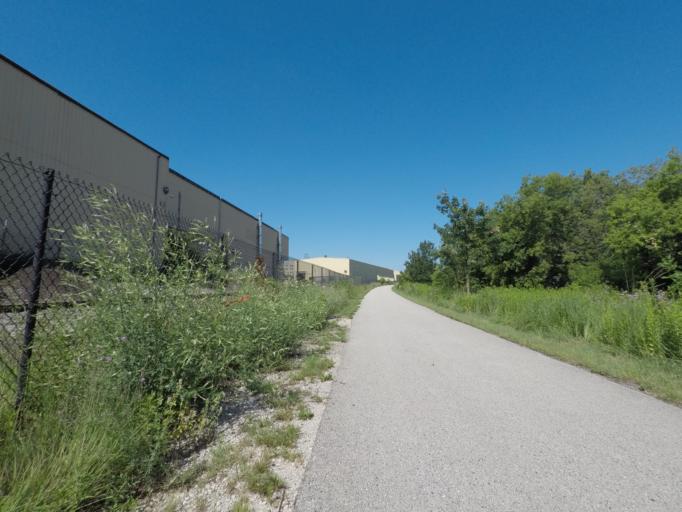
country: US
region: Wisconsin
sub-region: Milwaukee County
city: West Milwaukee
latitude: 43.0241
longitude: -87.9637
